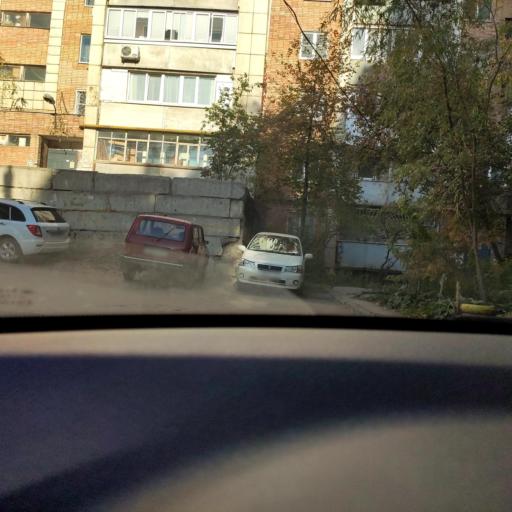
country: RU
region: Samara
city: Samara
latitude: 53.2163
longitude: 50.2217
